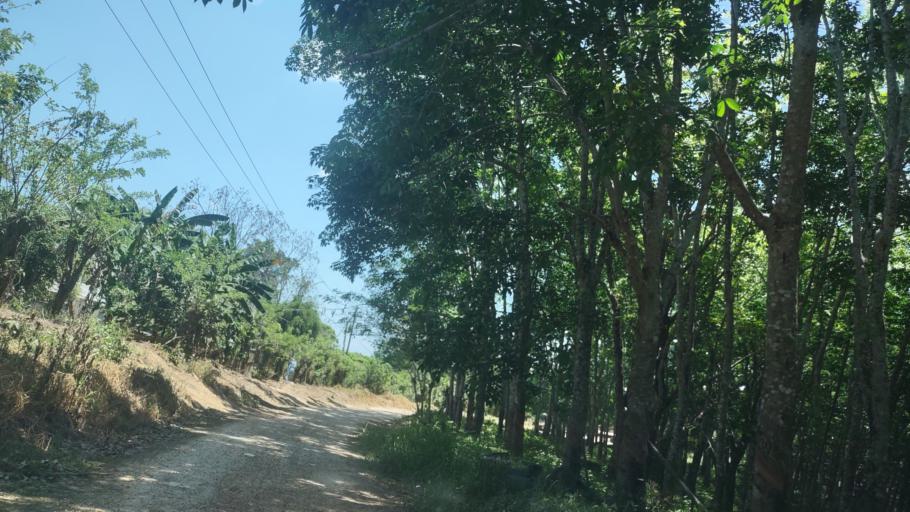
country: MX
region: Veracruz
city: Las Choapas
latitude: 17.7925
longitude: -94.1518
